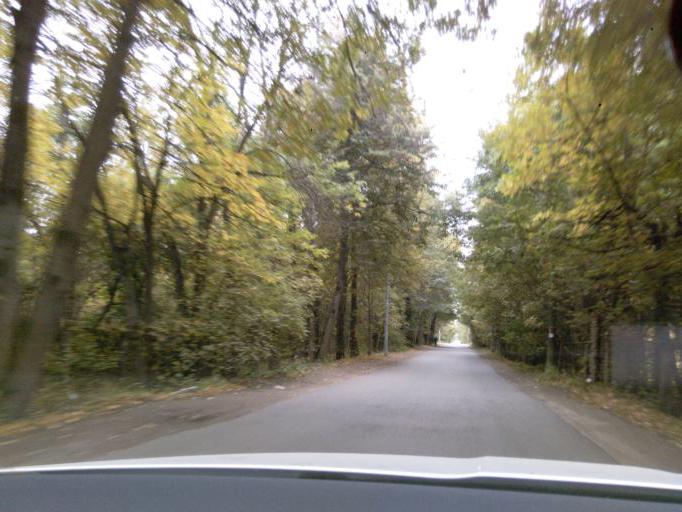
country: RU
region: Moscow
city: Severnyy
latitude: 55.9420
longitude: 37.5373
